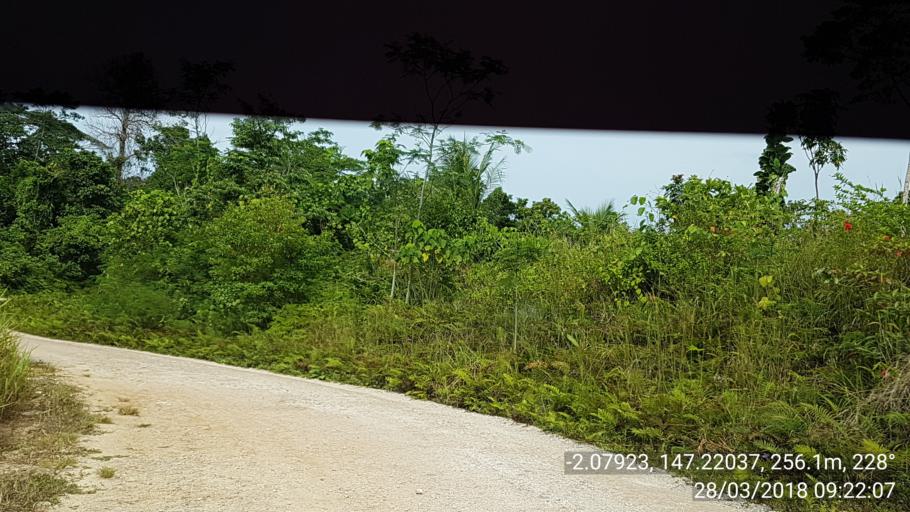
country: PG
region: Manus
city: Lorengau
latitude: -2.0792
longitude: 147.2206
